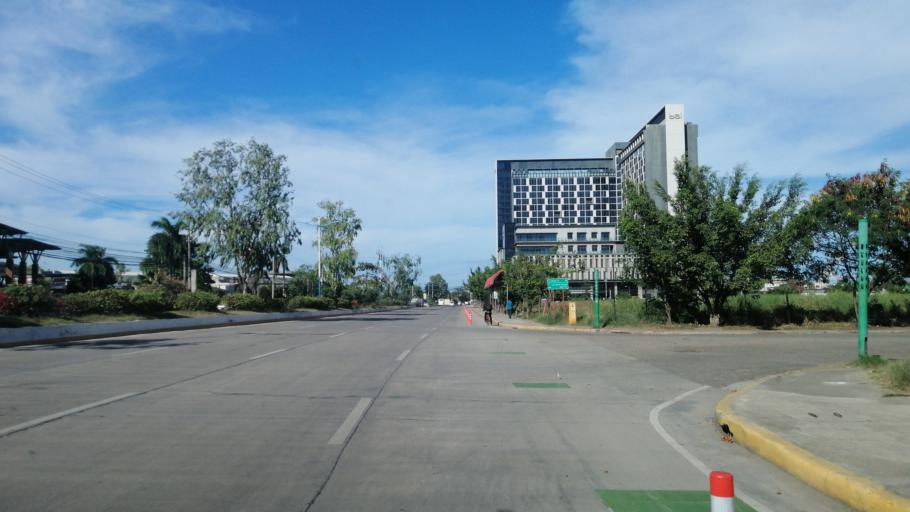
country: PH
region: Central Visayas
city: Mandaue City
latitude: 10.3235
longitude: 123.9344
